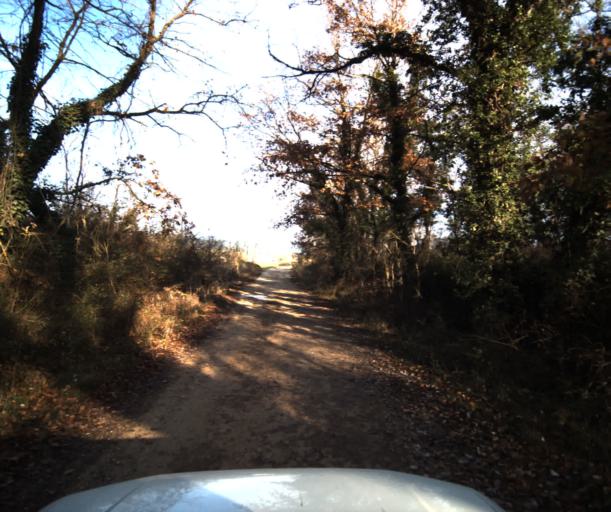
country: FR
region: Provence-Alpes-Cote d'Azur
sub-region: Departement des Bouches-du-Rhone
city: Le Puy-Sainte-Reparade
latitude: 43.6842
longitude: 5.4462
